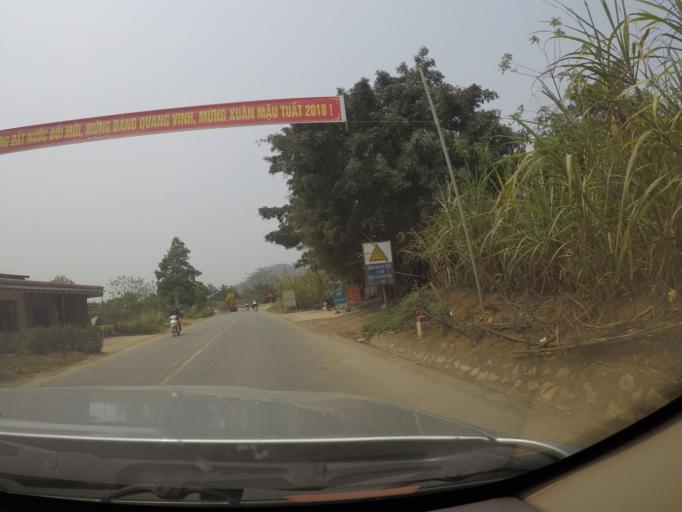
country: VN
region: Thanh Hoa
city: Thi Tran Cam Thuy
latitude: 20.1533
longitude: 105.4495
